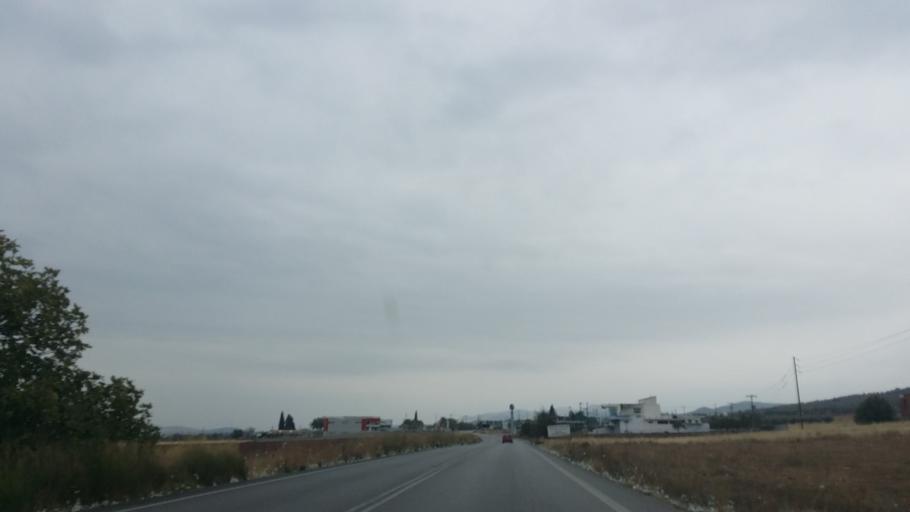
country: GR
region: Central Greece
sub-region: Nomos Voiotias
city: Thivai
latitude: 38.3271
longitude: 23.2787
